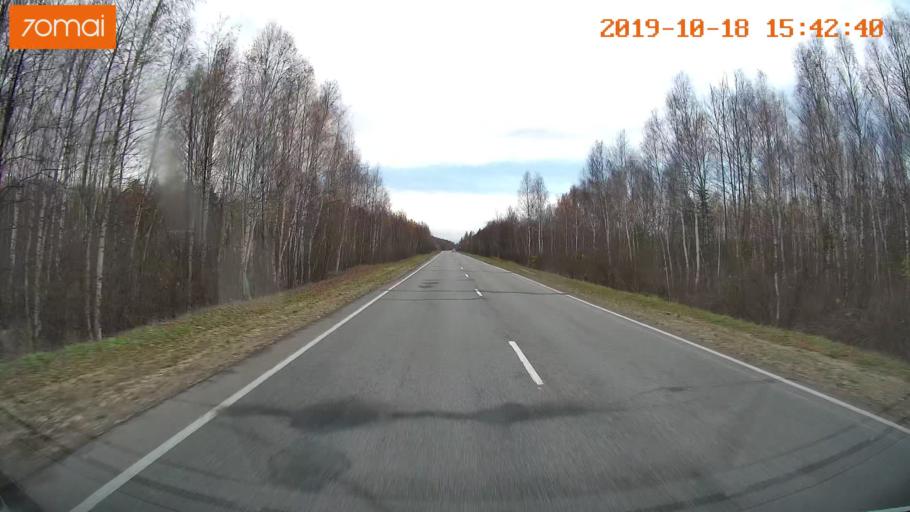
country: RU
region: Vladimir
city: Golovino
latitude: 55.9577
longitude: 40.5643
